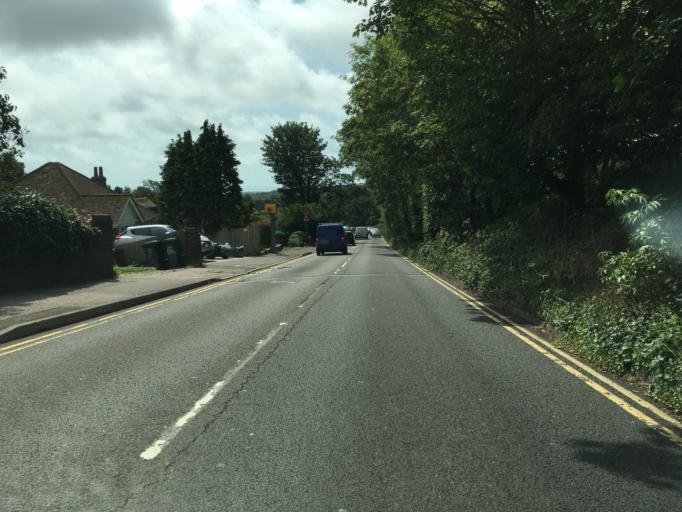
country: GB
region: England
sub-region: Brighton and Hove
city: Rottingdean
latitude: 50.8344
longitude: -0.0752
